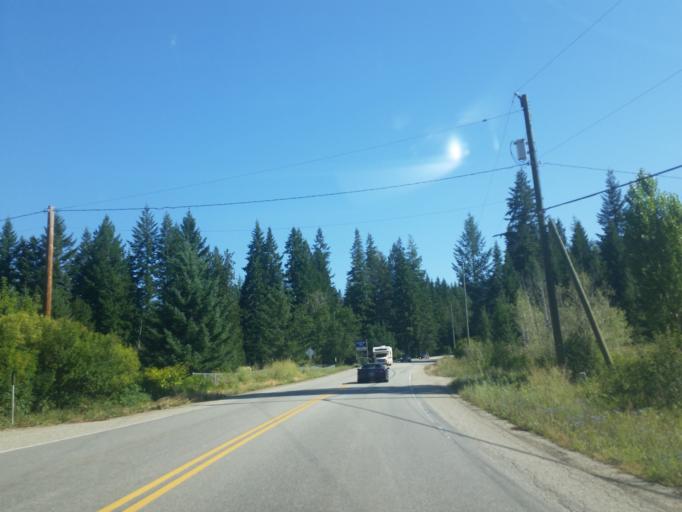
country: CA
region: British Columbia
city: Sicamous
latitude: 50.6948
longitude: -119.0426
